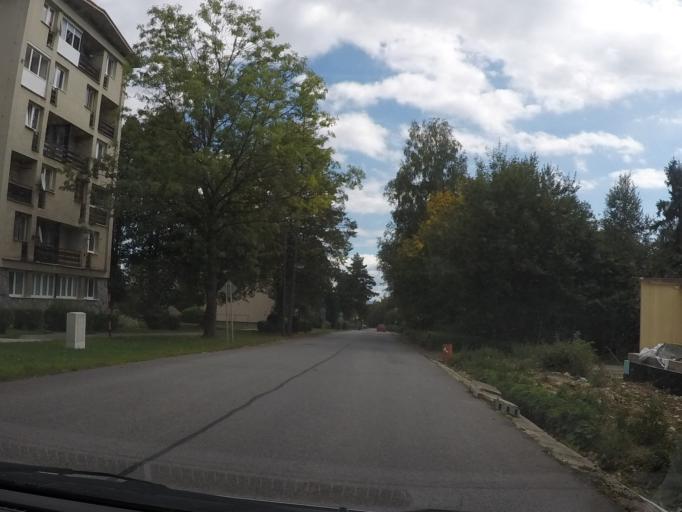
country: SK
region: Presovsky
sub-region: Okres Poprad
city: Nova Lesna
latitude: 49.1624
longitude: 20.2848
